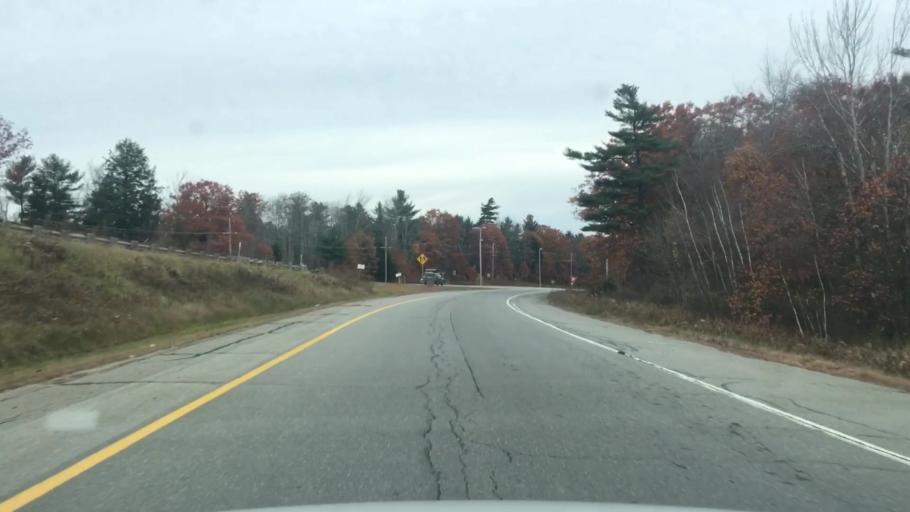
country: US
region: Maine
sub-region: Waldo County
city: Belfast
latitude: 44.4256
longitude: -69.0217
